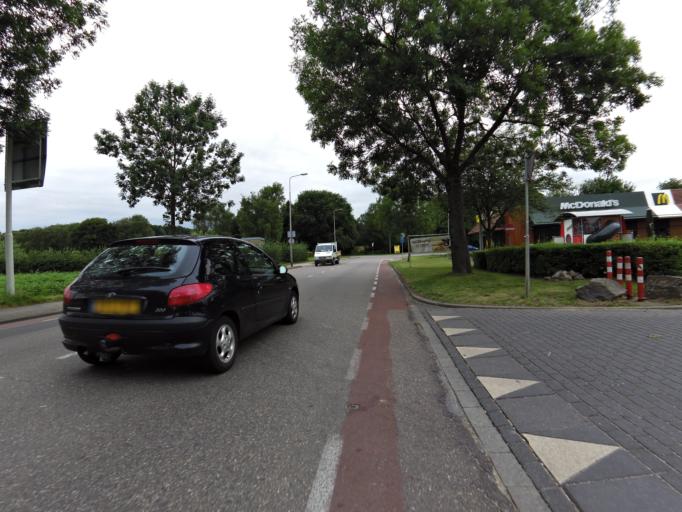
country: NL
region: Limburg
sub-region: Gemeente Heerlen
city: Heerlen
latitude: 50.9169
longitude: 6.0227
